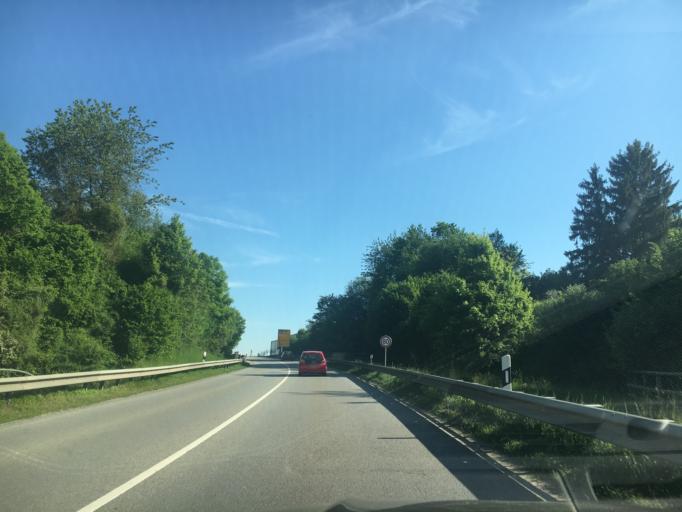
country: DE
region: Bavaria
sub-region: Upper Bavaria
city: Unterneukirchen
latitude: 48.1530
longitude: 12.6126
